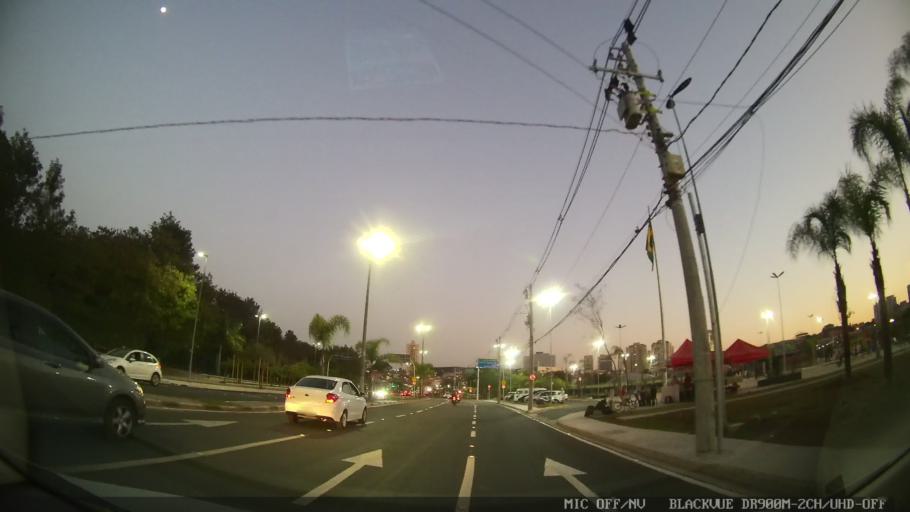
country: BR
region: Sao Paulo
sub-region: Barueri
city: Barueri
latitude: -23.4967
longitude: -46.8670
